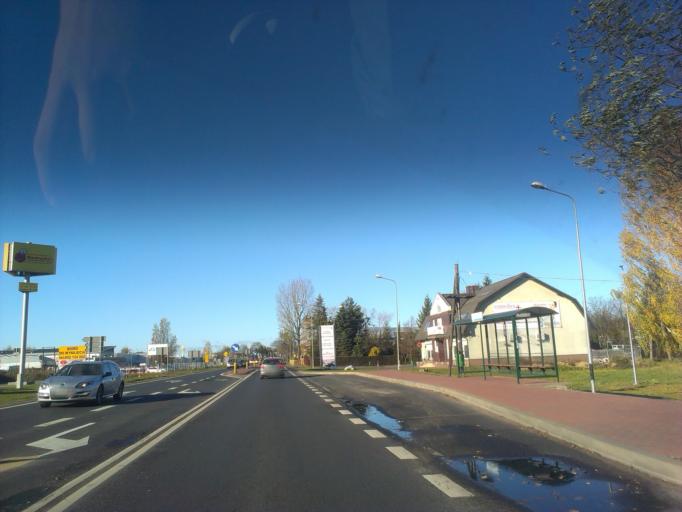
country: PL
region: Greater Poland Voivodeship
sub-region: Powiat poznanski
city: Suchy Las
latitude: 52.4762
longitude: 16.8725
